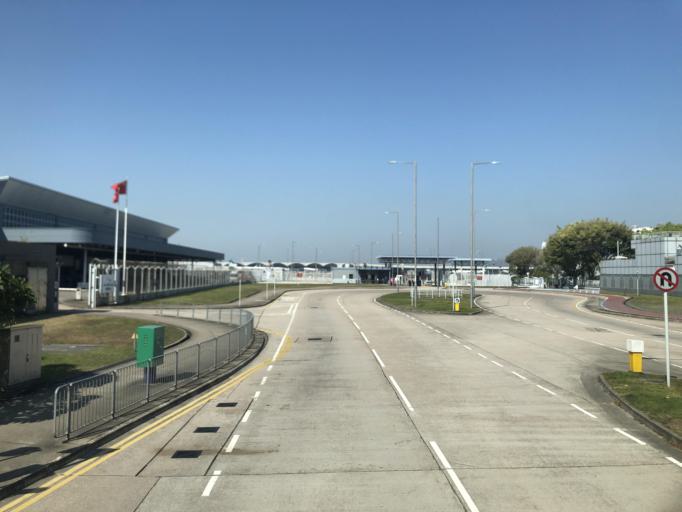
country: HK
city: Tai O
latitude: 22.3019
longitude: 113.9309
